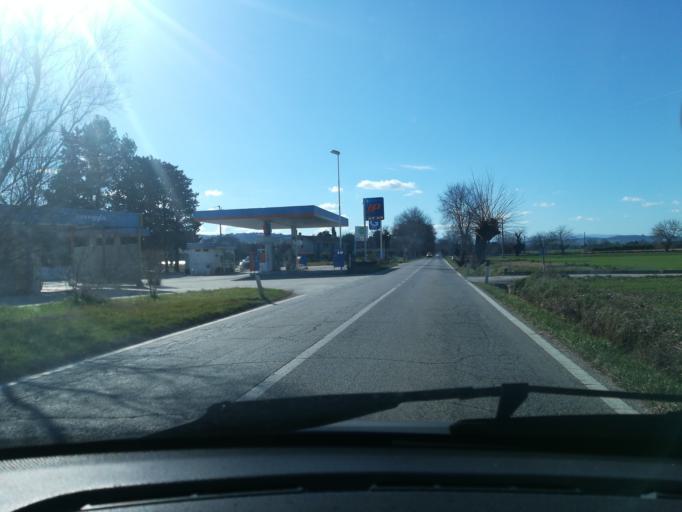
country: IT
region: The Marches
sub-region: Provincia di Macerata
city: Villa Potenza
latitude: 43.3387
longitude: 13.4295
